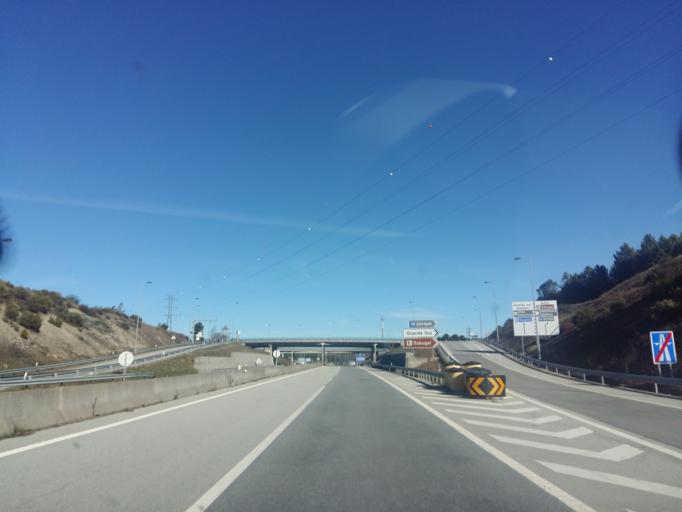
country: PT
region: Guarda
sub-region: Guarda
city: Sequeira
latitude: 40.5222
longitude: -7.2276
